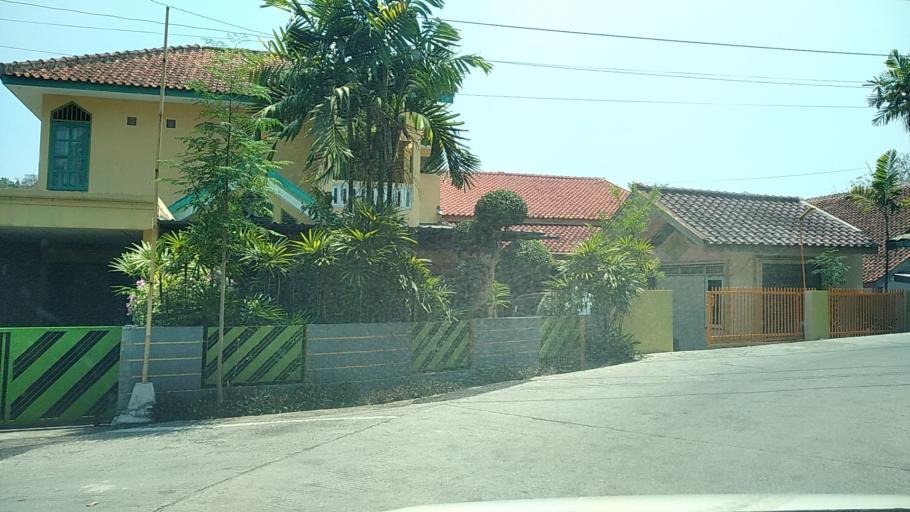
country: ID
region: Central Java
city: Semarang
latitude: -7.0196
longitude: 110.3797
